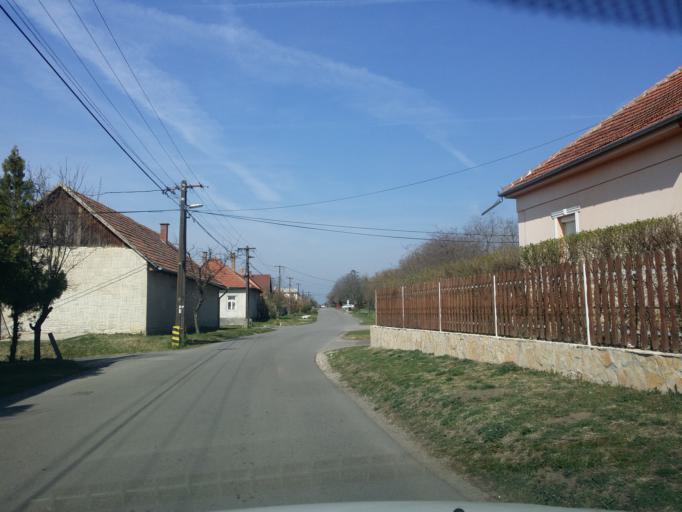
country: HU
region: Pest
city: Cegledbercel
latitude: 47.2189
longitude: 19.6760
